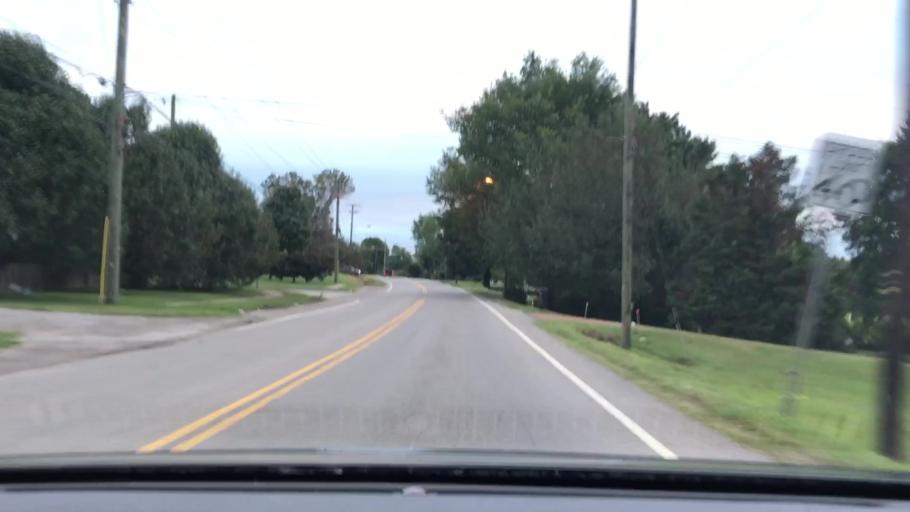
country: US
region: Tennessee
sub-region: Davidson County
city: Oak Hill
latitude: 36.0683
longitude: -86.7126
